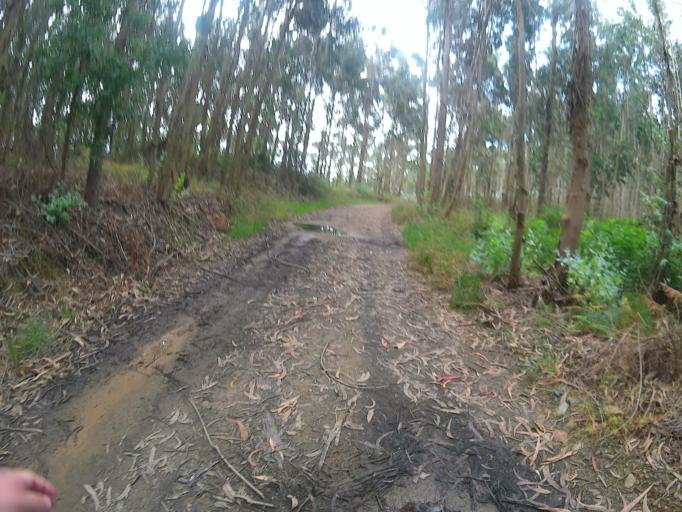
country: PT
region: Aveiro
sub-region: Albergaria-A-Velha
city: Branca
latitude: 40.7603
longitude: -8.4325
